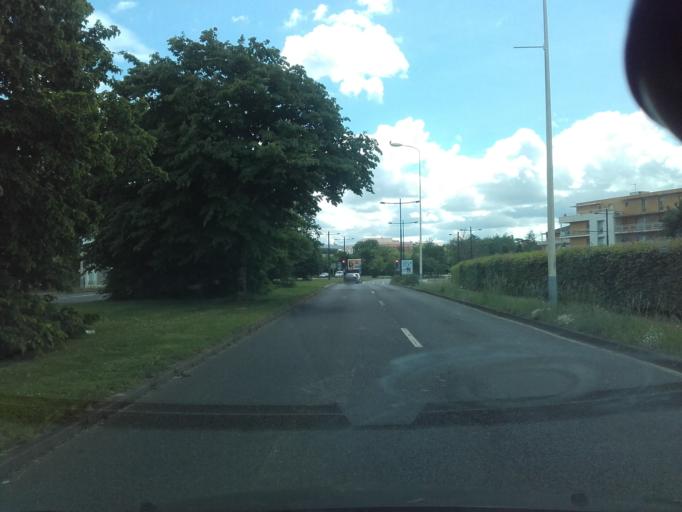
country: FR
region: Centre
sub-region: Departement d'Indre-et-Loire
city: Saint-Cyr-sur-Loire
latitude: 47.4216
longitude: 0.7022
